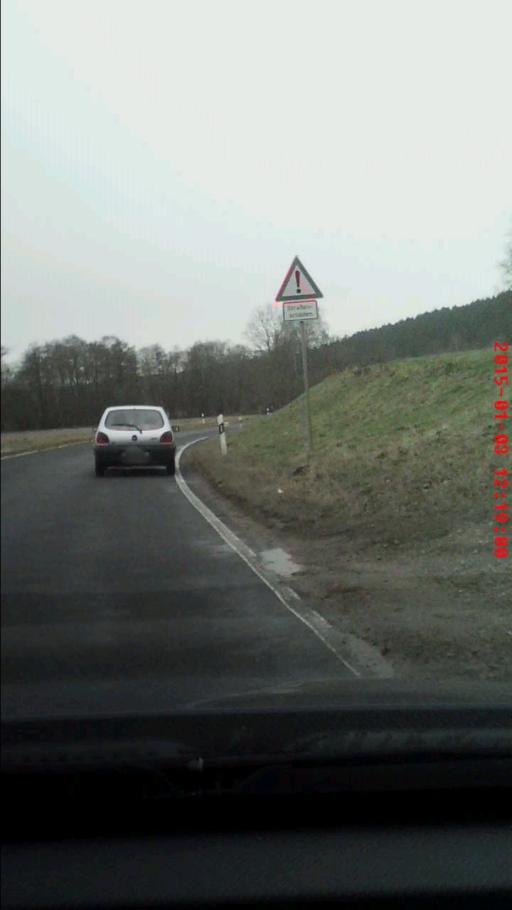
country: DE
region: Thuringia
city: Rittersdorf
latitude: 50.8515
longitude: 11.2681
